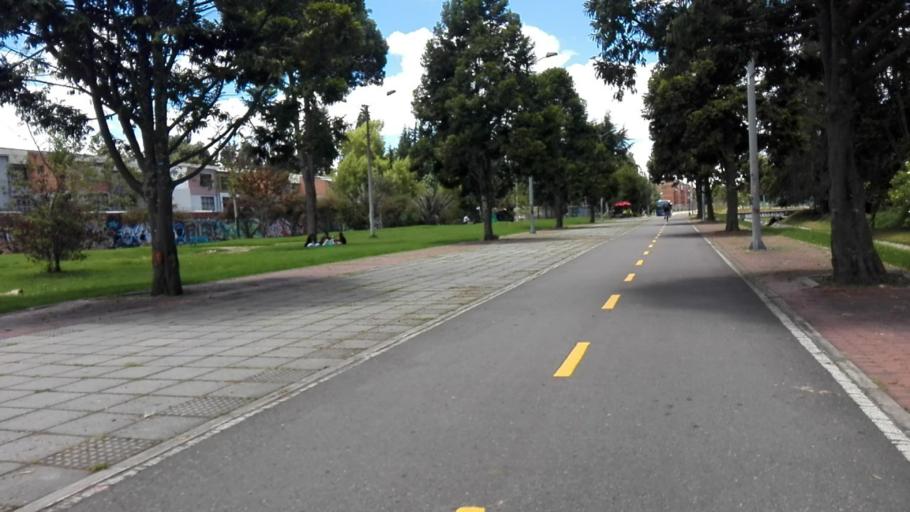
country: CO
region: Cundinamarca
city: Cota
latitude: 4.7318
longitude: -74.1188
